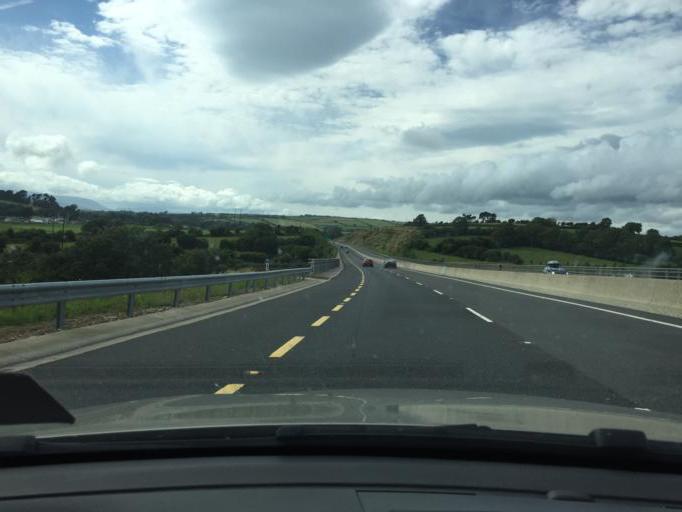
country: IE
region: Leinster
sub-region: Kilkenny
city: Mooncoin
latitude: 52.2378
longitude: -7.2364
